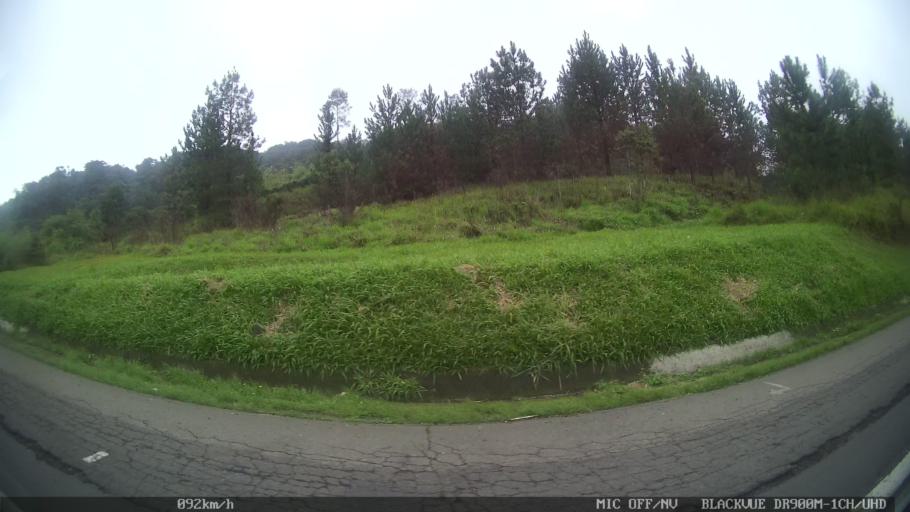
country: BR
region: Parana
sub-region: Antonina
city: Antonina
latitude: -25.0814
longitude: -48.6216
